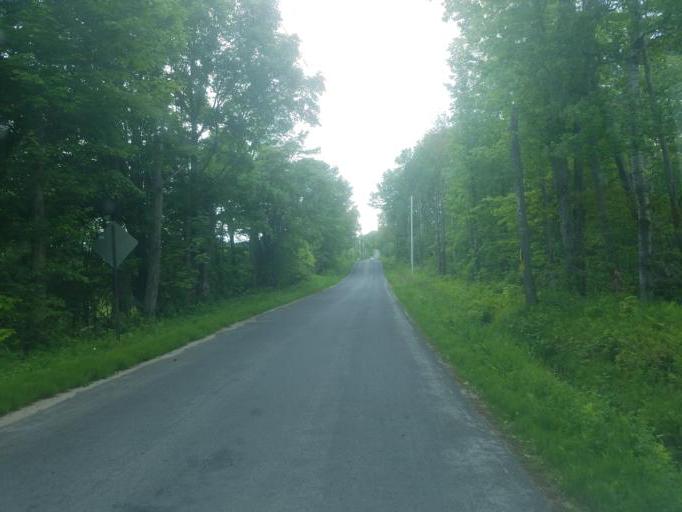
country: US
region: New York
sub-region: Herkimer County
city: Herkimer
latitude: 43.2168
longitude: -74.9539
